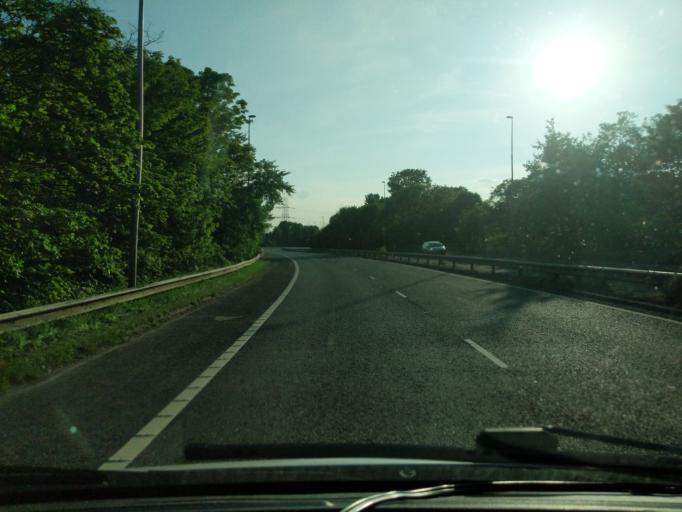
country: GB
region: England
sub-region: Cheshire West and Chester
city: Frodsham
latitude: 53.3180
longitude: -2.7326
